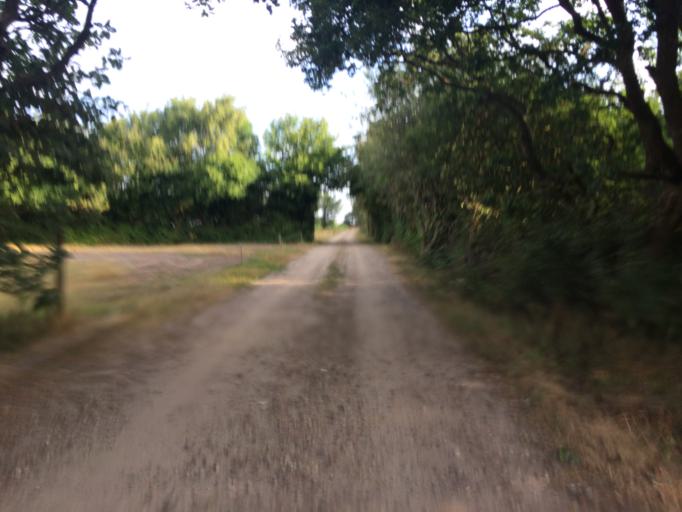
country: DK
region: Central Jutland
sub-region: Holstebro Kommune
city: Vinderup
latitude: 56.6145
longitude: 8.7154
